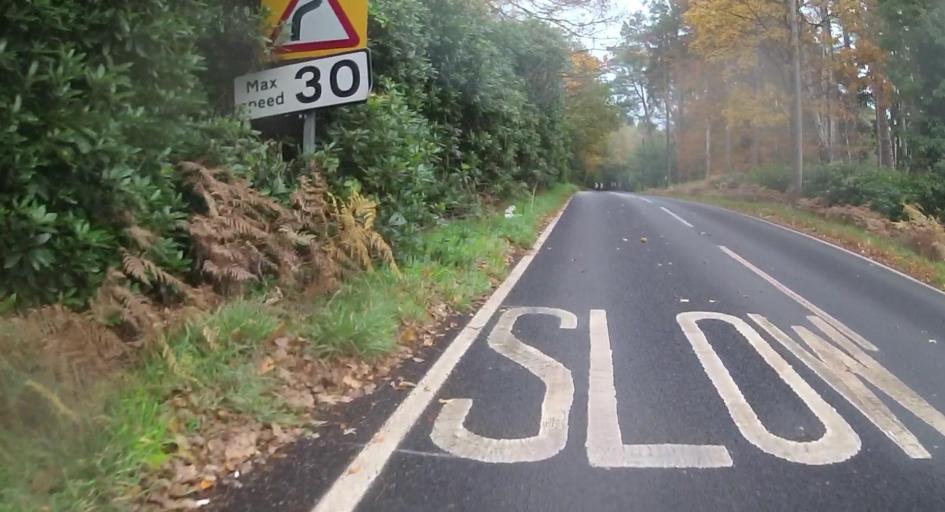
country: GB
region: England
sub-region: Wokingham
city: Finchampstead
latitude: 51.3675
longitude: -0.8451
